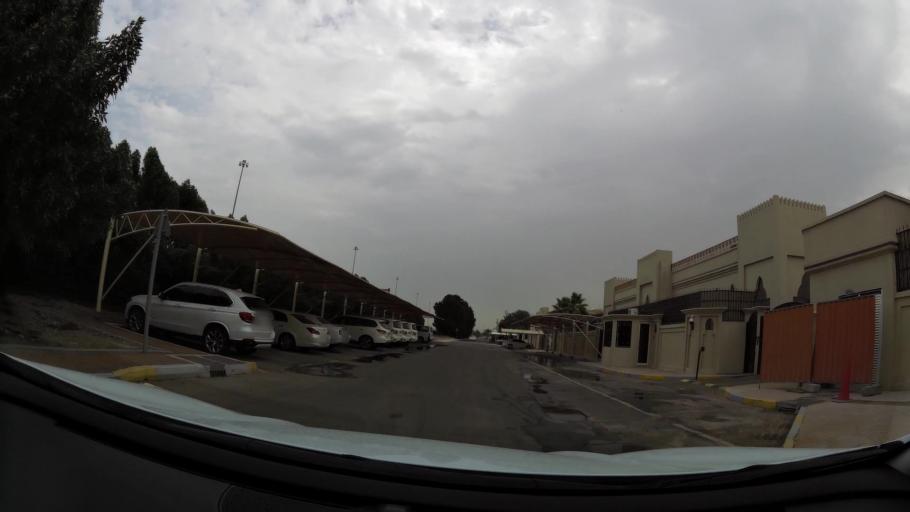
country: AE
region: Abu Dhabi
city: Abu Dhabi
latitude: 24.4429
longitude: 54.4432
